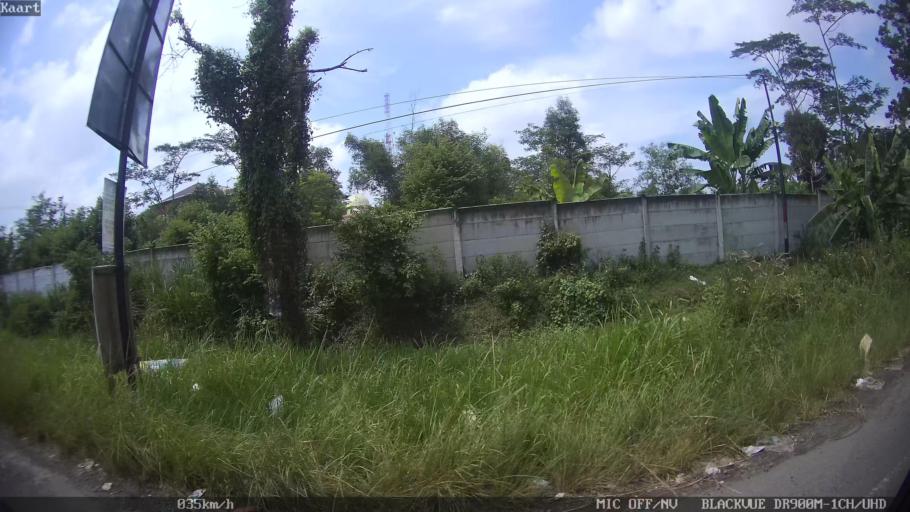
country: ID
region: Lampung
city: Kedaton
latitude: -5.3586
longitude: 105.3066
